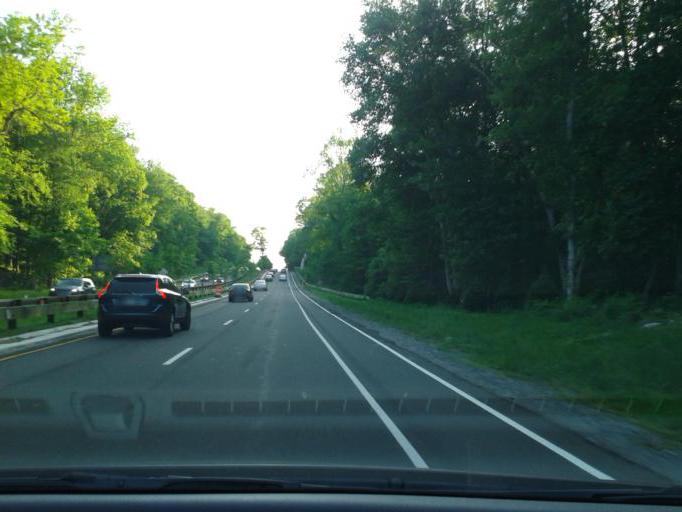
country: US
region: Connecticut
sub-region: Fairfield County
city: North Stamford
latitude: 41.1004
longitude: -73.5960
